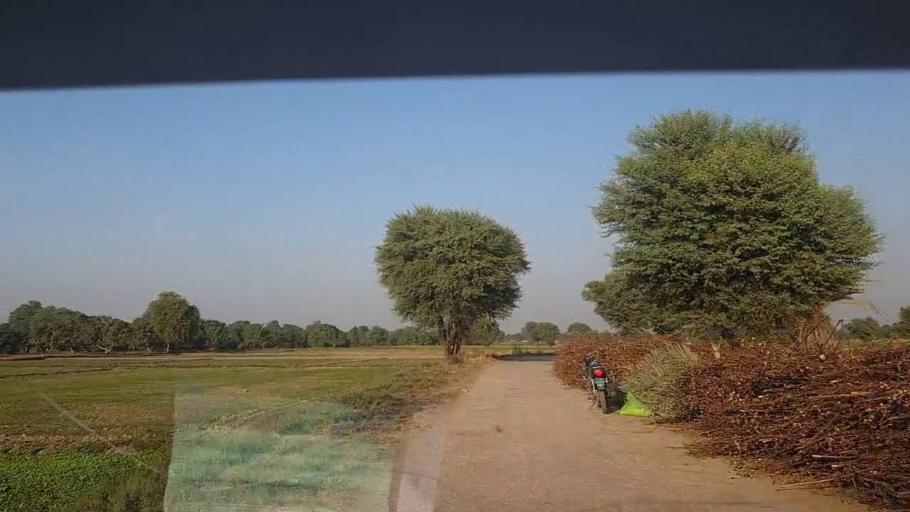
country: PK
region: Sindh
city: Sobhadero
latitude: 27.3022
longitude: 68.4205
